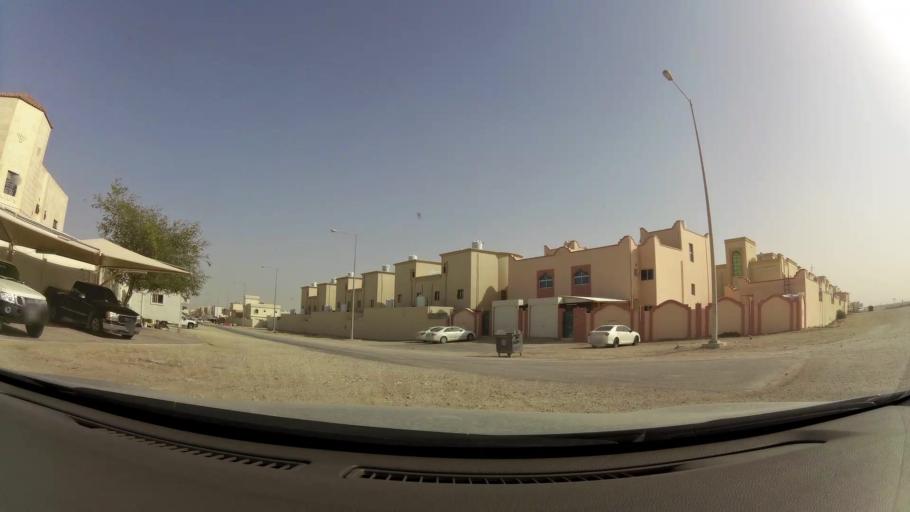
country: QA
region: Baladiyat ar Rayyan
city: Ar Rayyan
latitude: 25.3425
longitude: 51.4196
